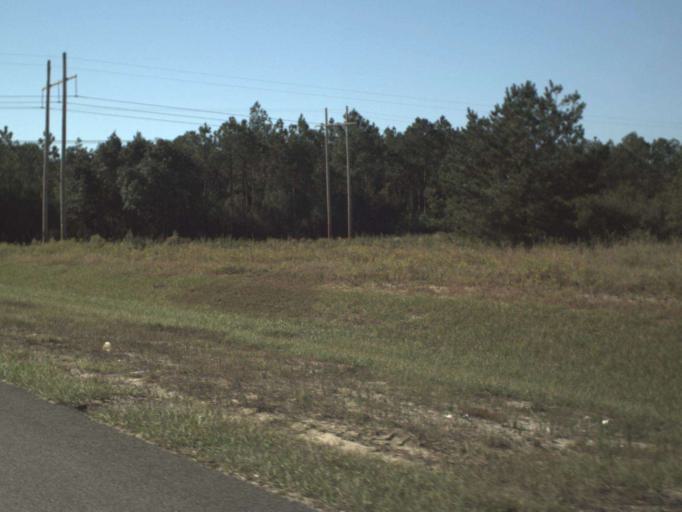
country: US
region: Florida
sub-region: Walton County
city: Freeport
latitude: 30.5315
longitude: -86.1080
